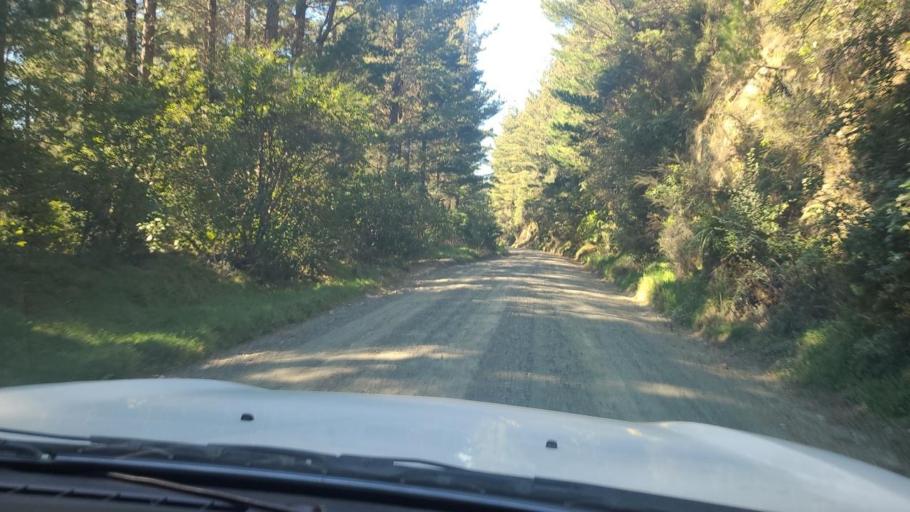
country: NZ
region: Hawke's Bay
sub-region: Napier City
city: Taradale
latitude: -39.4081
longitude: 176.4753
